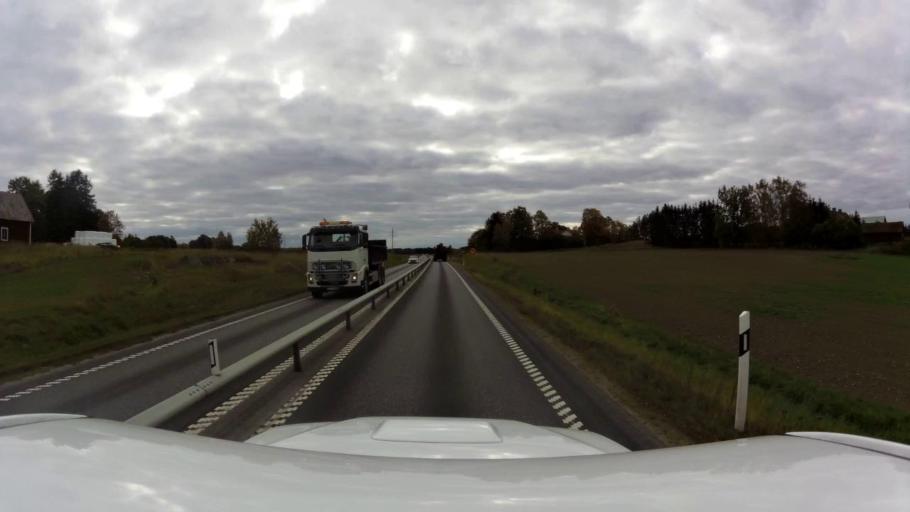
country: SE
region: OEstergoetland
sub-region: Linkopings Kommun
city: Malmslatt
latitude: 58.3363
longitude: 15.5573
